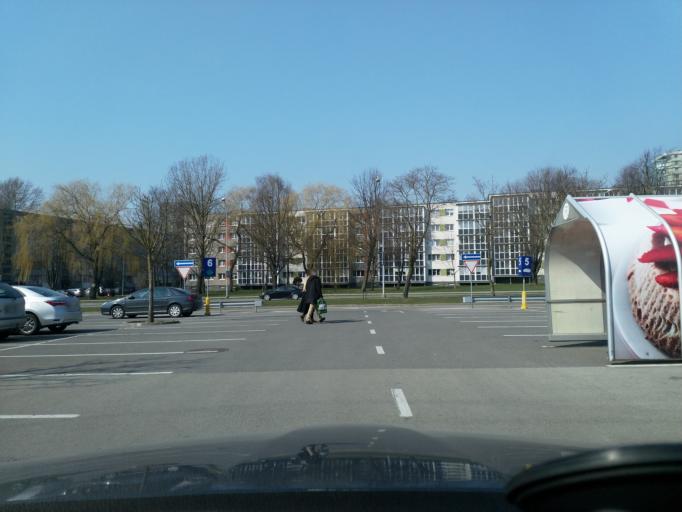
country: LT
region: Klaipedos apskritis
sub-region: Klaipeda
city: Klaipeda
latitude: 55.6940
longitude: 21.1546
